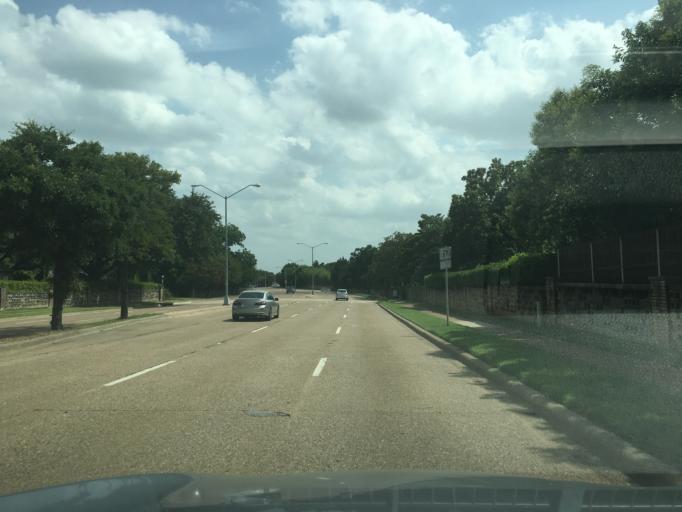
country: US
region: Texas
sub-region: Dallas County
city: University Park
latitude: 32.8982
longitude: -96.8192
